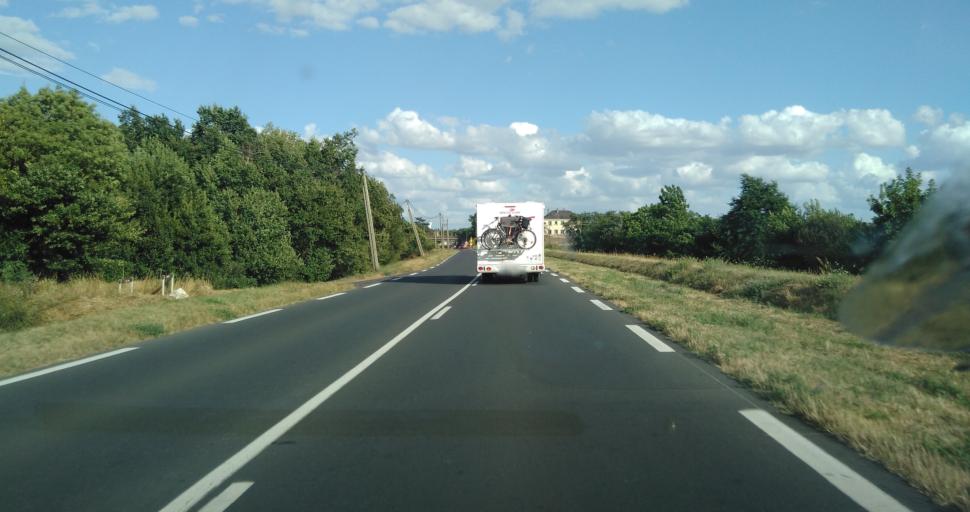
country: FR
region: Centre
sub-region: Departement d'Indre-et-Loire
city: Montlouis-sur-Loire
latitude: 47.3996
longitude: 0.8175
